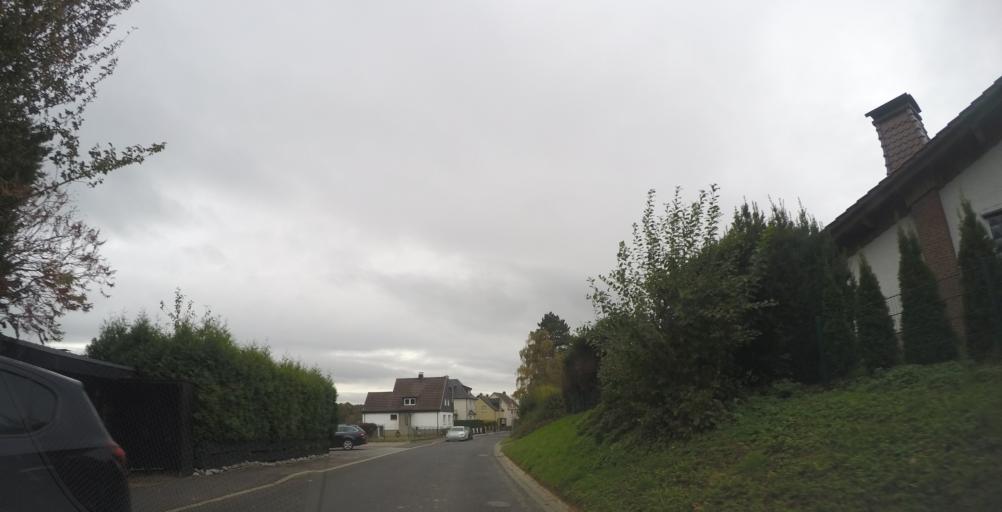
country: DE
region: North Rhine-Westphalia
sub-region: Regierungsbezirk Arnsberg
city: Unna
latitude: 51.4834
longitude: 7.6993
